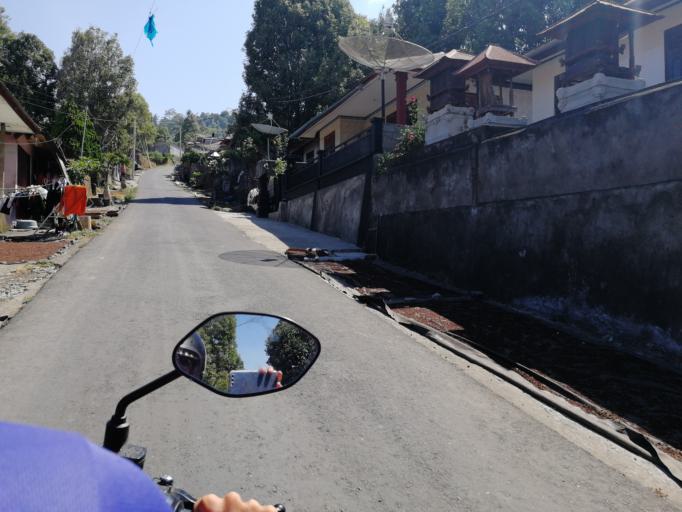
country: ID
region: Bali
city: Banjar Kedisan
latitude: -8.1660
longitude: 115.3033
